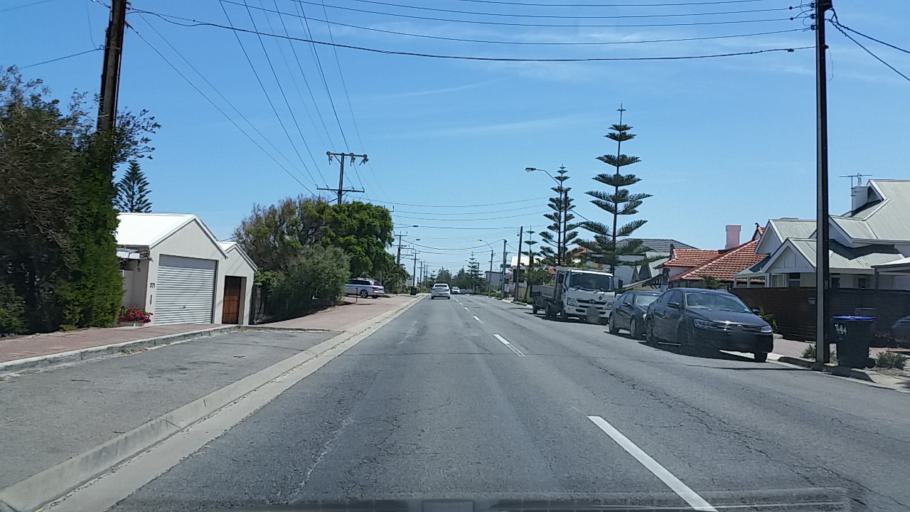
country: AU
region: South Australia
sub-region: Charles Sturt
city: Henley Beach
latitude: -34.9120
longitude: 138.4923
